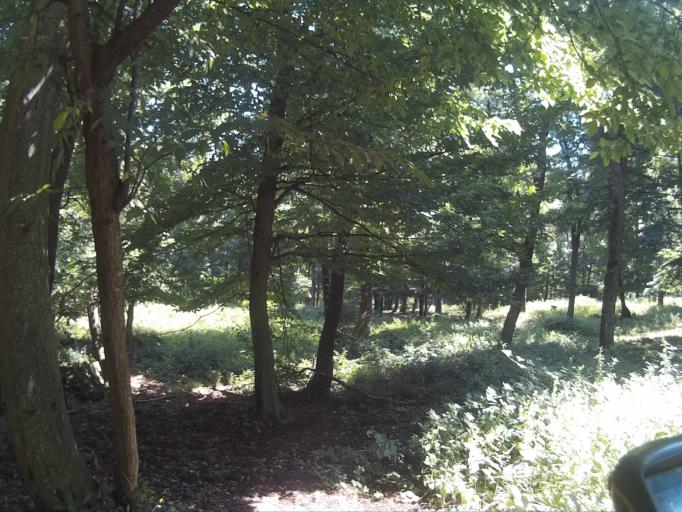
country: HU
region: Veszprem
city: Zirc
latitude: 47.1784
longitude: 17.8678
